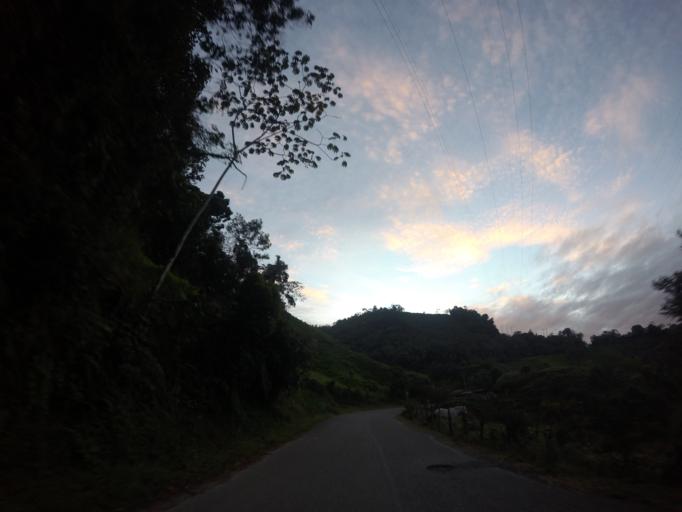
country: CO
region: Caldas
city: Manzanares
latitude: 5.2707
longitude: -75.1251
